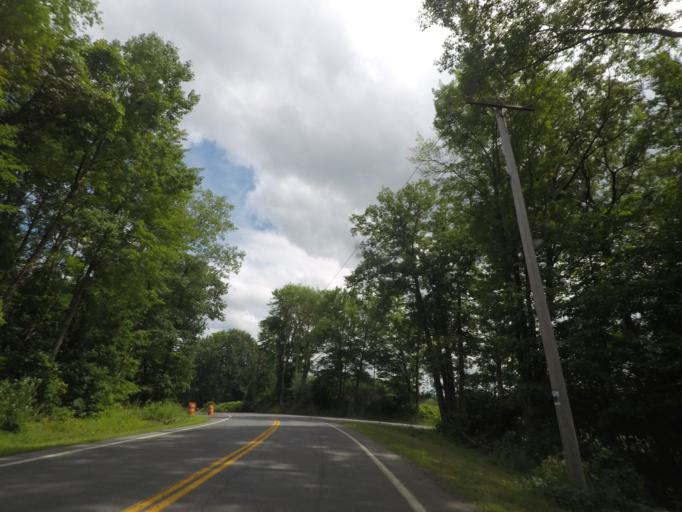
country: US
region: New York
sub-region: Saratoga County
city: Stillwater
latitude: 43.0243
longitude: -73.7022
